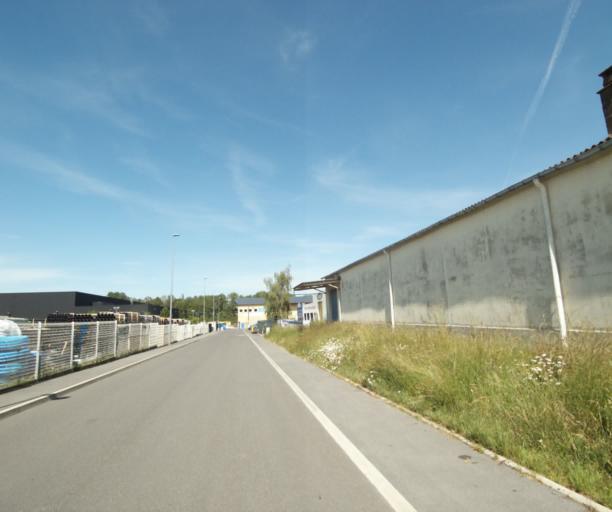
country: FR
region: Champagne-Ardenne
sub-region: Departement des Ardennes
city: Villers-Semeuse
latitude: 49.7367
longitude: 4.7330
